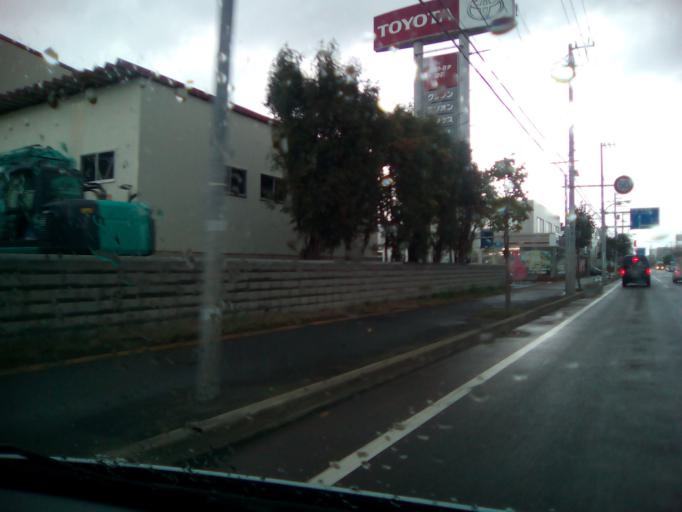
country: JP
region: Hokkaido
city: Sapporo
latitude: 43.0299
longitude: 141.4436
